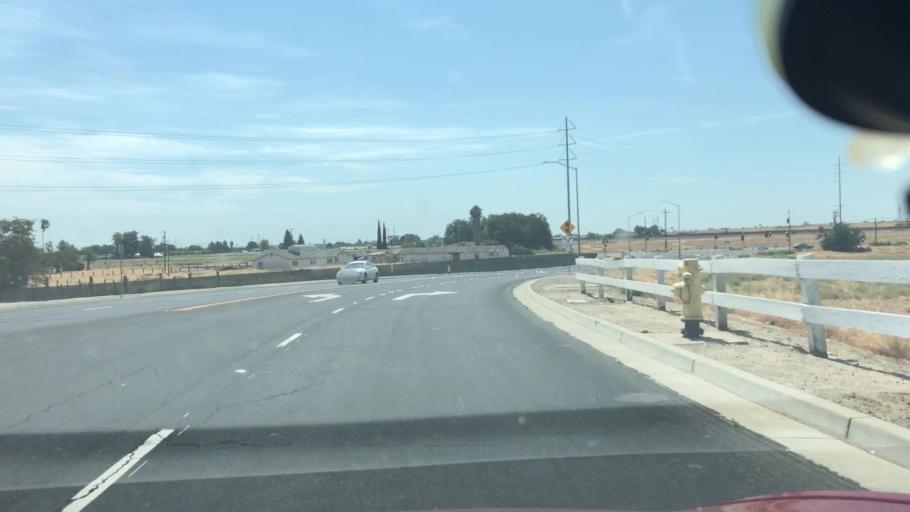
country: US
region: California
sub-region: San Joaquin County
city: Lathrop
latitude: 37.7968
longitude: -121.2794
